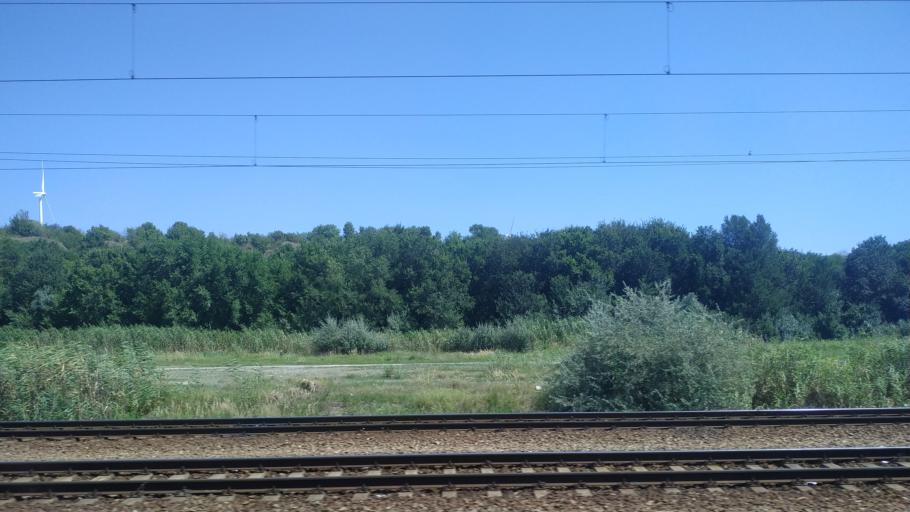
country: RO
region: Constanta
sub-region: Comuna Saligny
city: Saligny
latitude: 44.2876
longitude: 28.0776
